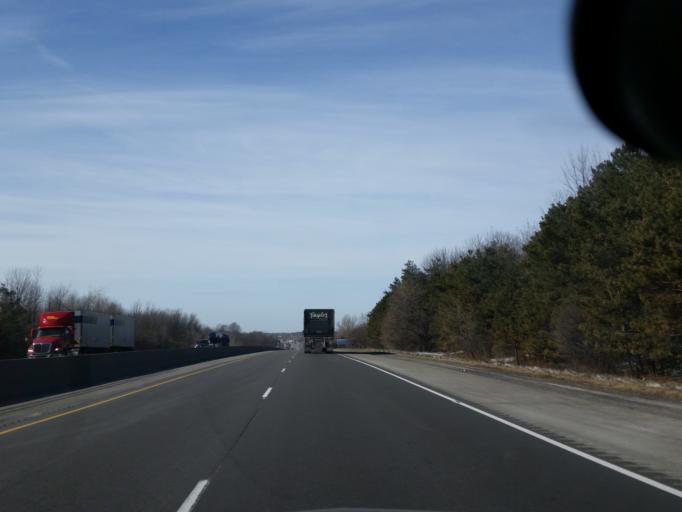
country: CA
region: Ontario
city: Brockville
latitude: 44.6250
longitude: -75.6644
